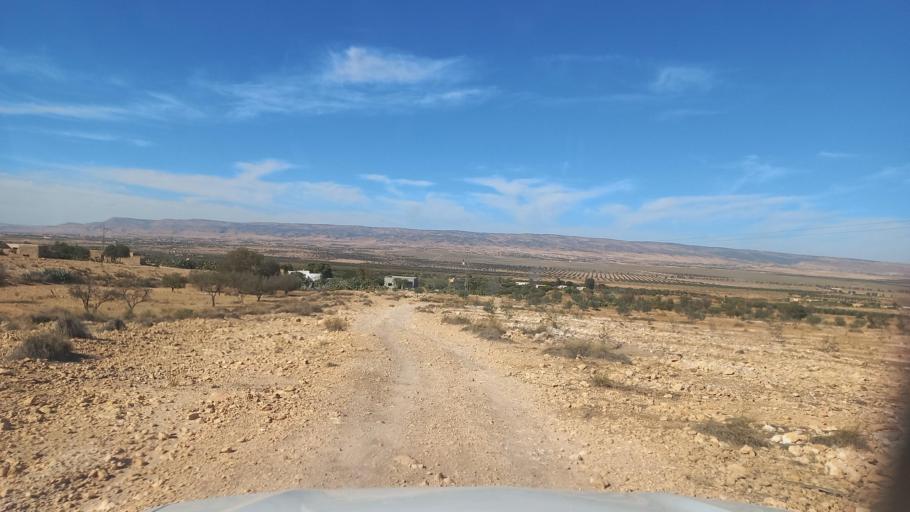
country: TN
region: Al Qasrayn
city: Kasserine
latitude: 35.2000
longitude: 8.9727
